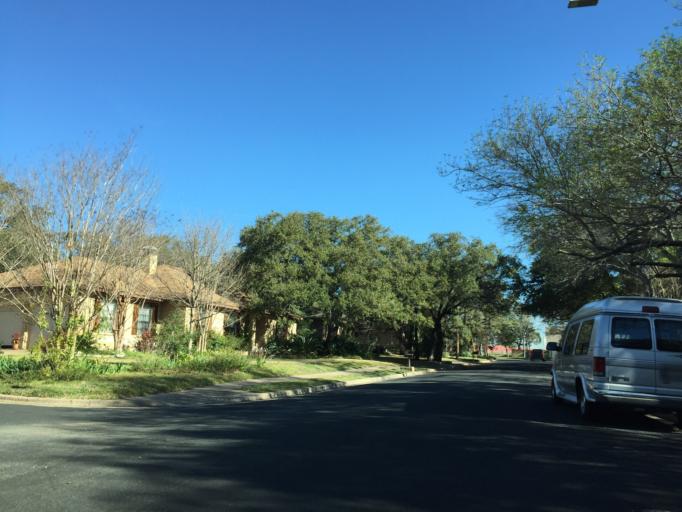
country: US
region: Texas
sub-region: Williamson County
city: Jollyville
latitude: 30.4044
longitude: -97.7312
